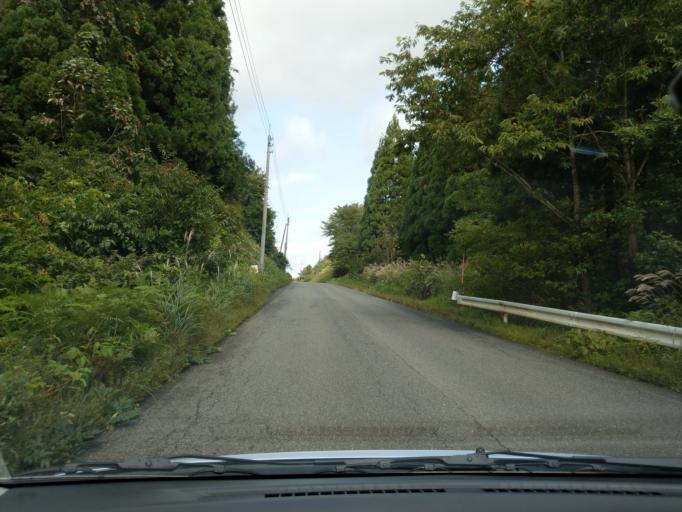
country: JP
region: Akita
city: Omagari
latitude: 39.4544
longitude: 140.3218
